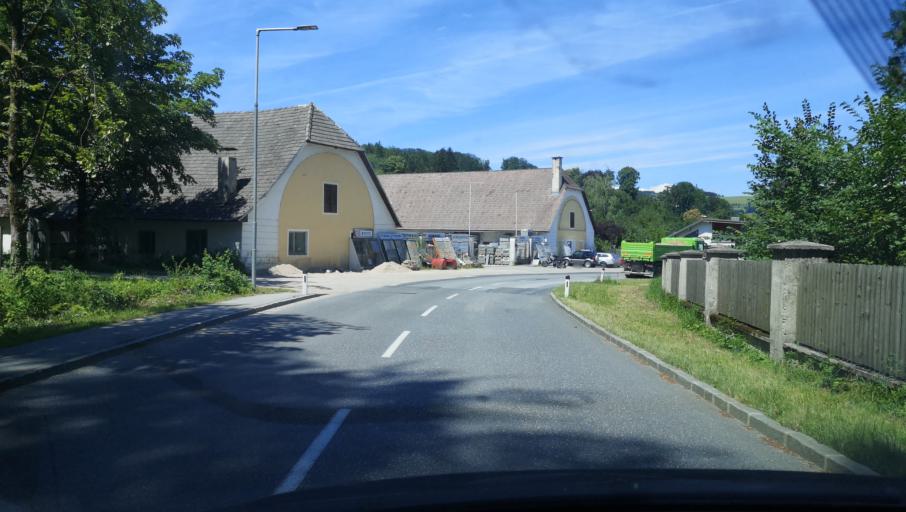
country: AT
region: Lower Austria
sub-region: Politischer Bezirk Scheibbs
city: Gresten
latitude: 47.9751
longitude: 15.0206
